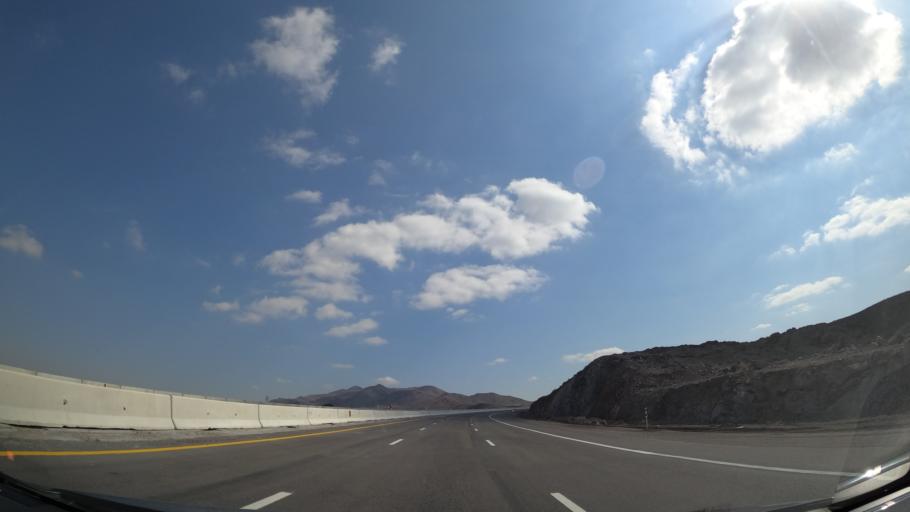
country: IR
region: Alborz
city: Nazarabad
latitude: 35.6959
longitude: 50.6299
